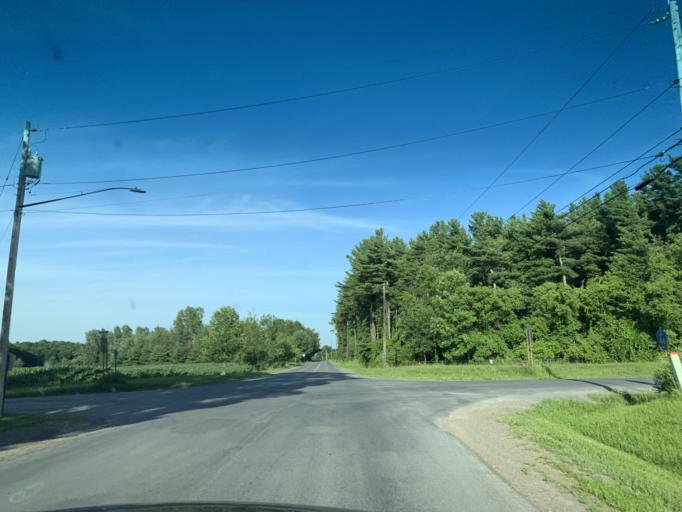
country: US
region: New York
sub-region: Oneida County
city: Clinton
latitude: 43.0546
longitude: -75.4463
